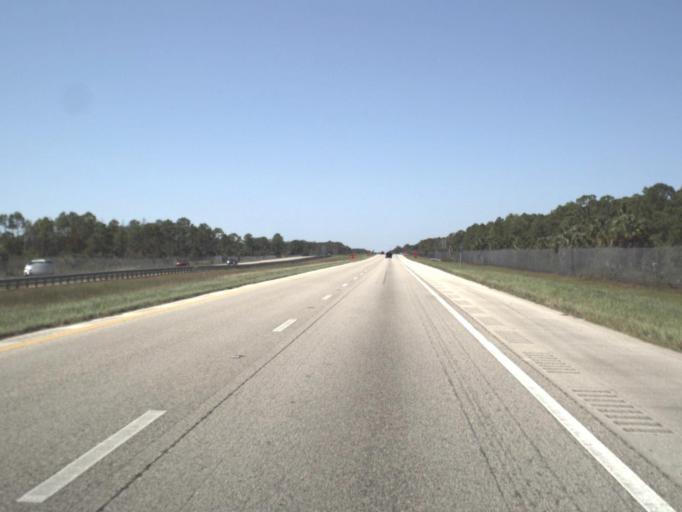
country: US
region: Florida
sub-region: Collier County
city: Orangetree
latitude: 26.1548
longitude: -81.3560
